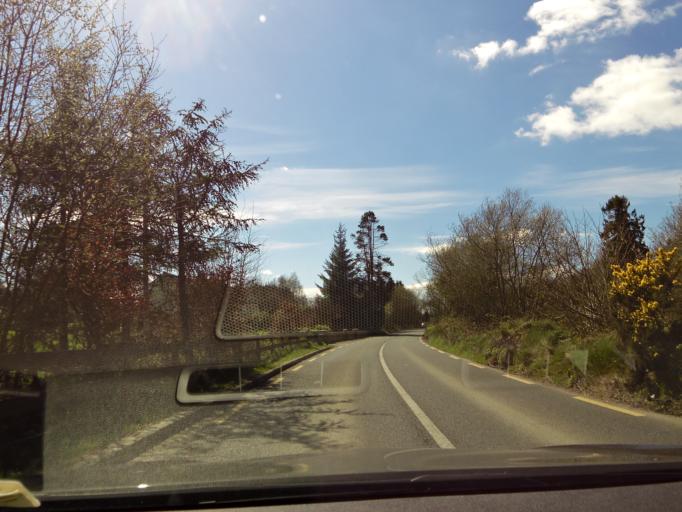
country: IE
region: Leinster
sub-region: Wicklow
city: Aughrim
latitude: 52.8513
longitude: -6.3326
